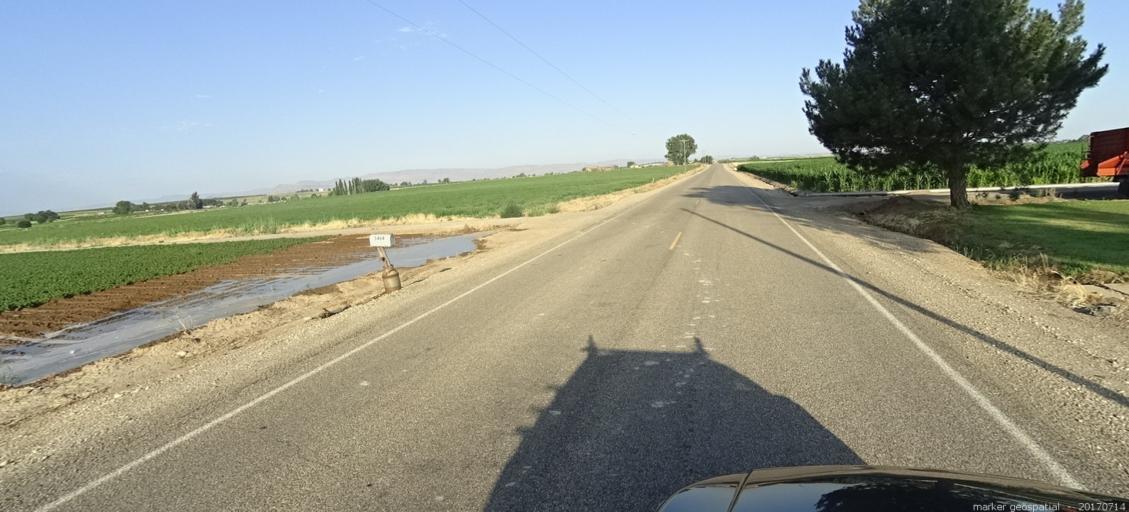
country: US
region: Idaho
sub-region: Ada County
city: Kuna
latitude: 43.4593
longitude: -116.5031
